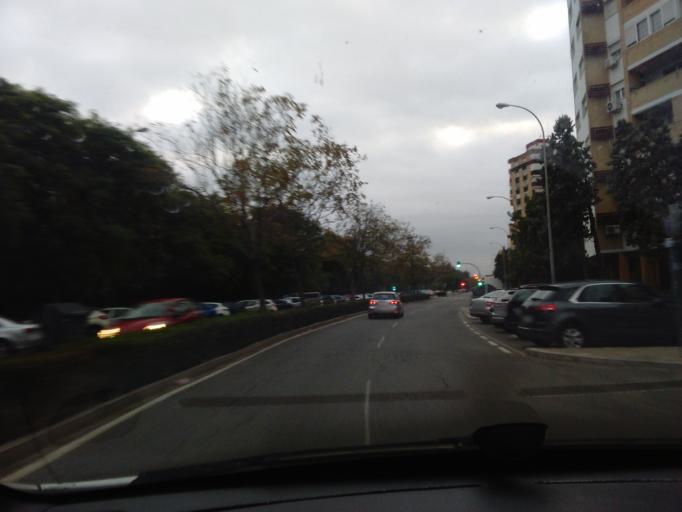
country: ES
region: Andalusia
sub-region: Provincia de Sevilla
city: Sevilla
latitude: 37.3850
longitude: -5.9441
